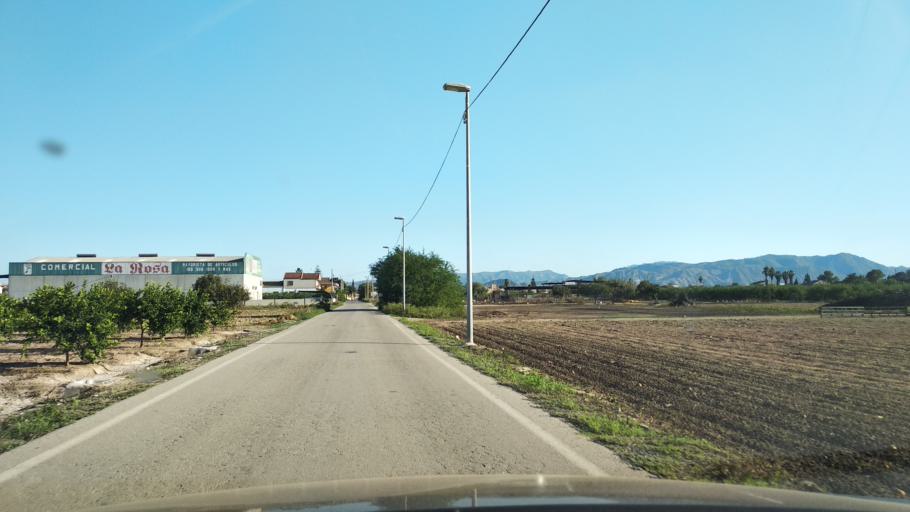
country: ES
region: Murcia
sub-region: Murcia
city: Santomera
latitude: 38.0429
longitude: -1.0356
